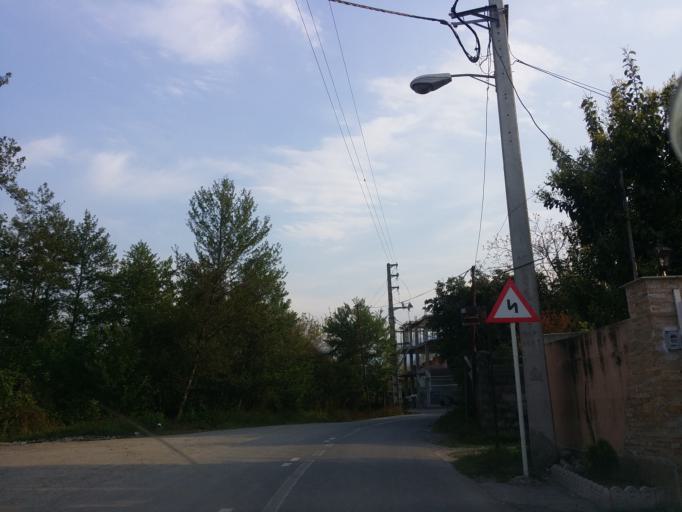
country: IR
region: Mazandaran
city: Chalus
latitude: 36.6846
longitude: 51.3722
